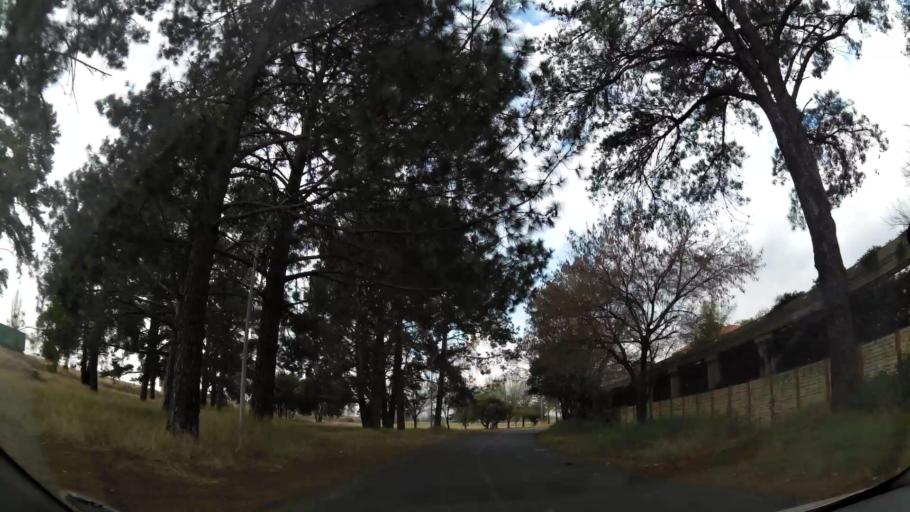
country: ZA
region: Orange Free State
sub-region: Fezile Dabi District Municipality
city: Sasolburg
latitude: -26.7894
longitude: 27.8196
